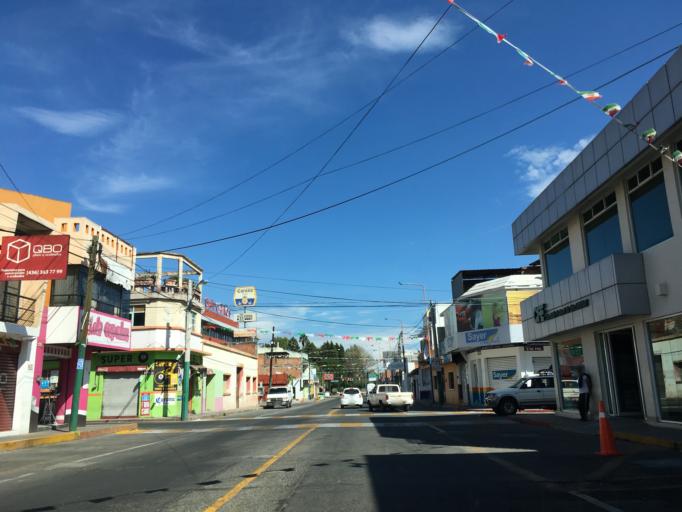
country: MX
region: Michoacan
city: Zacapu
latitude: 19.8150
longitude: -101.7851
